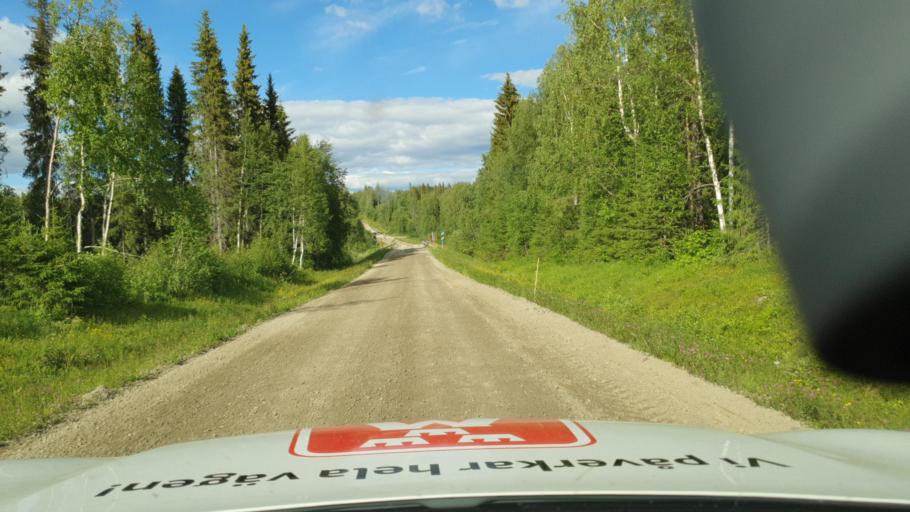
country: SE
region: Vaesterbotten
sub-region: Lycksele Kommun
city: Lycksele
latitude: 64.3693
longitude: 18.5699
